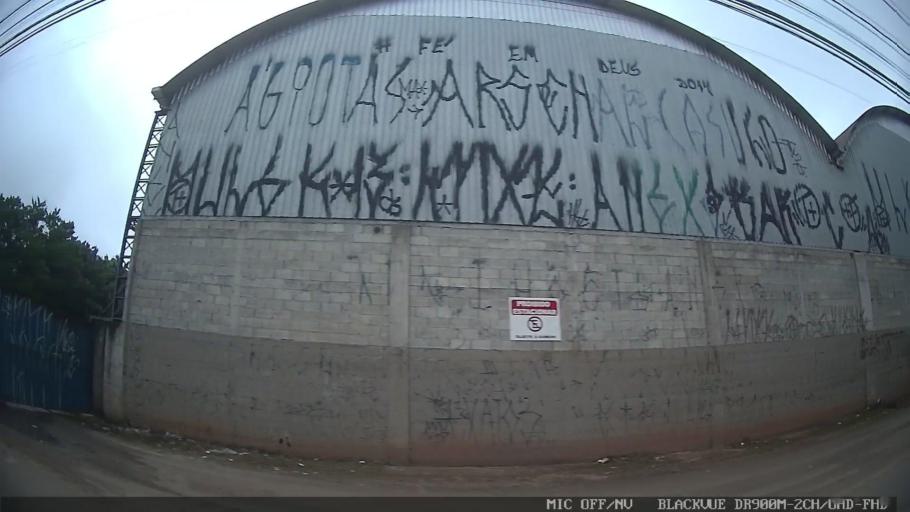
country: BR
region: Sao Paulo
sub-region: Mogi das Cruzes
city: Mogi das Cruzes
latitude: -23.5034
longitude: -46.1648
